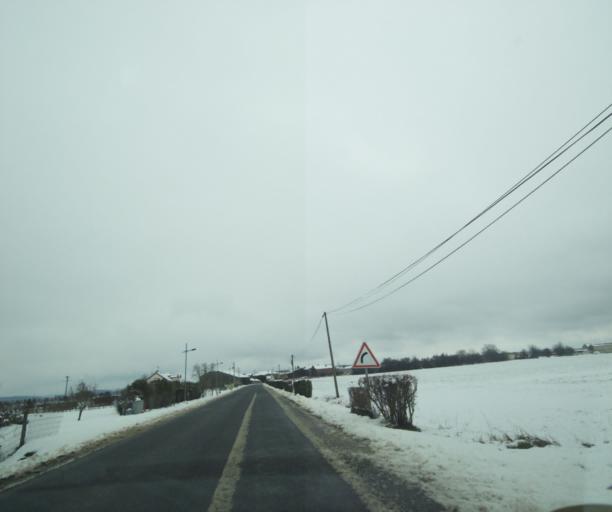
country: FR
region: Champagne-Ardenne
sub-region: Departement de la Haute-Marne
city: Montier-en-Der
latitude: 48.4436
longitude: 4.8023
